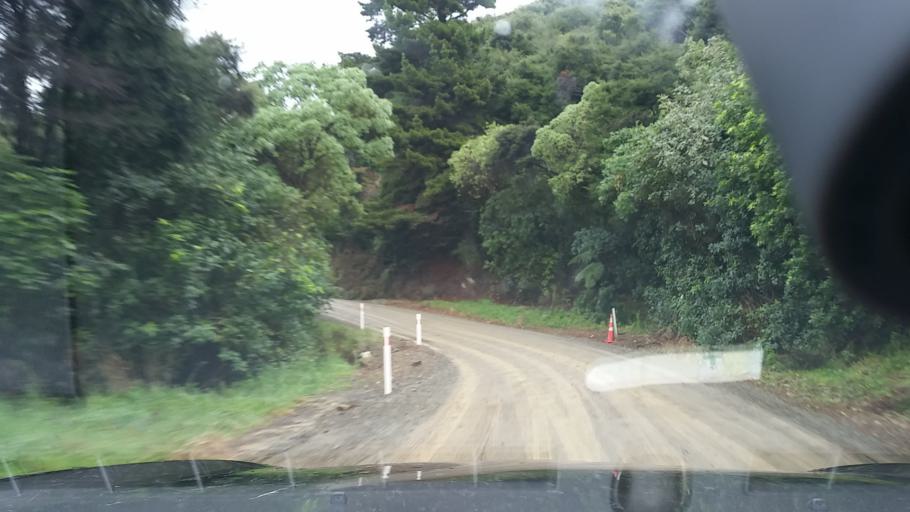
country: NZ
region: Marlborough
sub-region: Marlborough District
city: Picton
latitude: -41.3716
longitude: 174.0645
